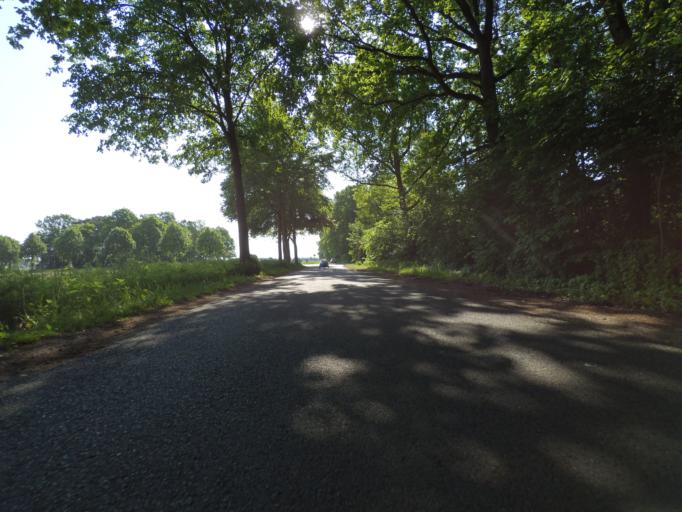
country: DE
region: Lower Saxony
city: Burgdorf
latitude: 52.4185
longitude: 10.0115
